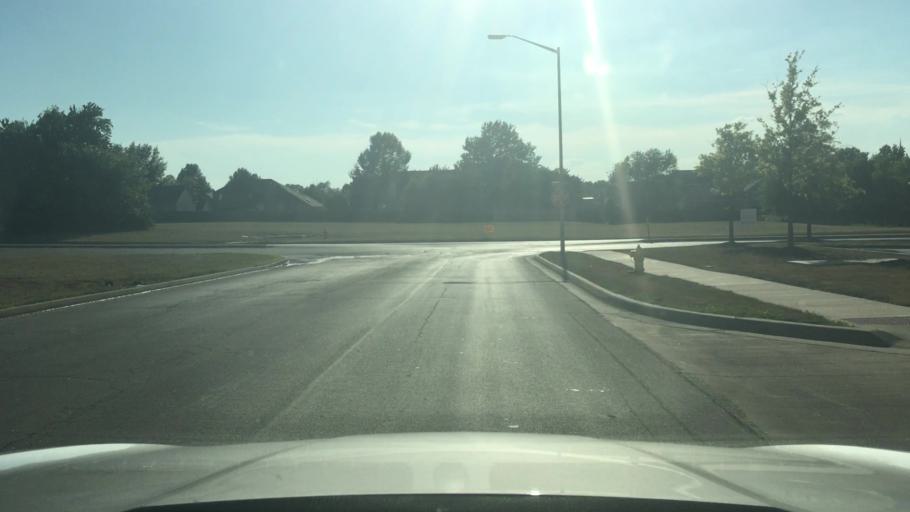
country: US
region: Missouri
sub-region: Cass County
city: Lake Winnebago
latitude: 38.8515
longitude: -94.3830
